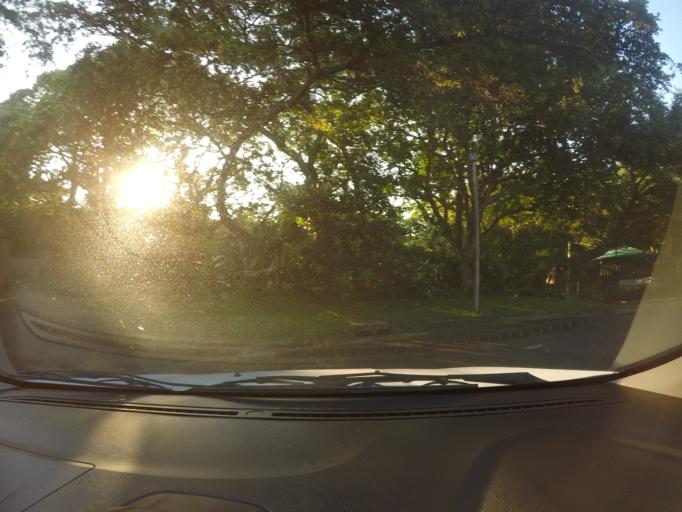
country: ZA
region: KwaZulu-Natal
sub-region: uThungulu District Municipality
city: Richards Bay
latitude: -28.7813
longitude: 32.0950
